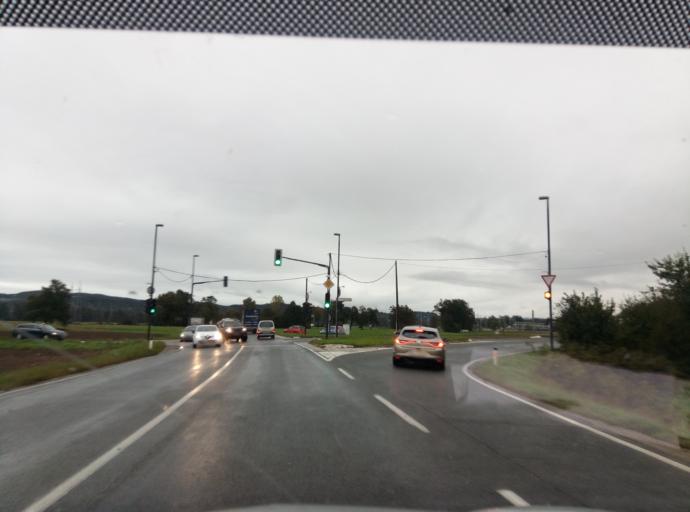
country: SI
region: Ljubljana
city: Ljubljana
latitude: 46.1036
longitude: 14.4777
